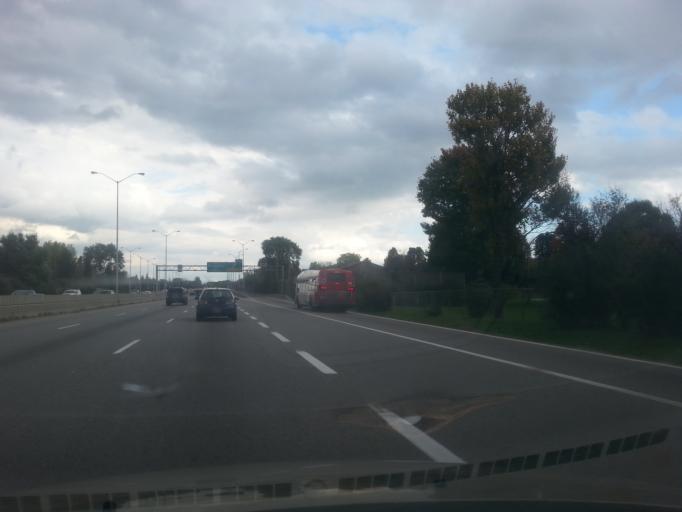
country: CA
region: Ontario
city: Bells Corners
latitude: 45.3563
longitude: -75.7770
